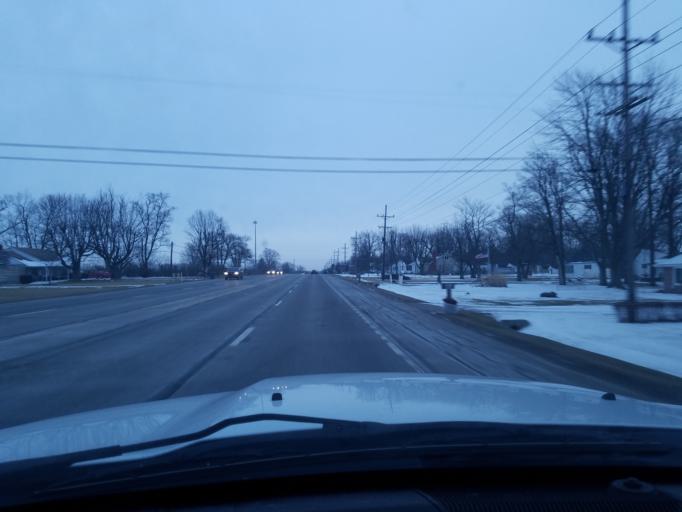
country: US
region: Indiana
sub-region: Delaware County
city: Muncie
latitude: 40.1933
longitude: -85.3034
